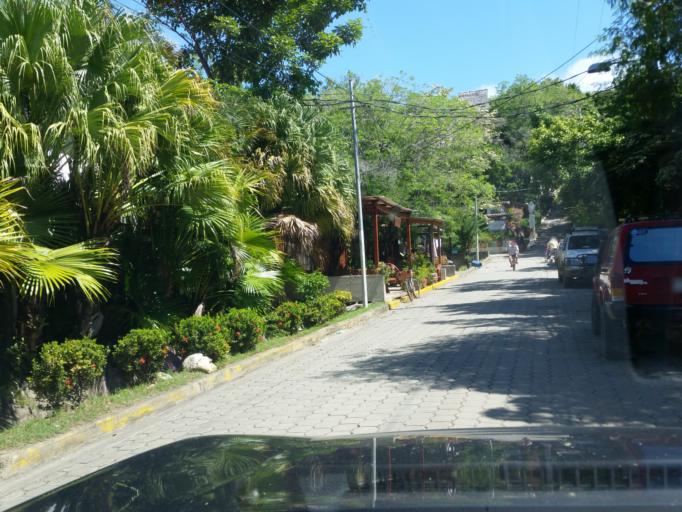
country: NI
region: Rivas
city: San Juan del Sur
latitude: 11.2529
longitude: -85.8692
